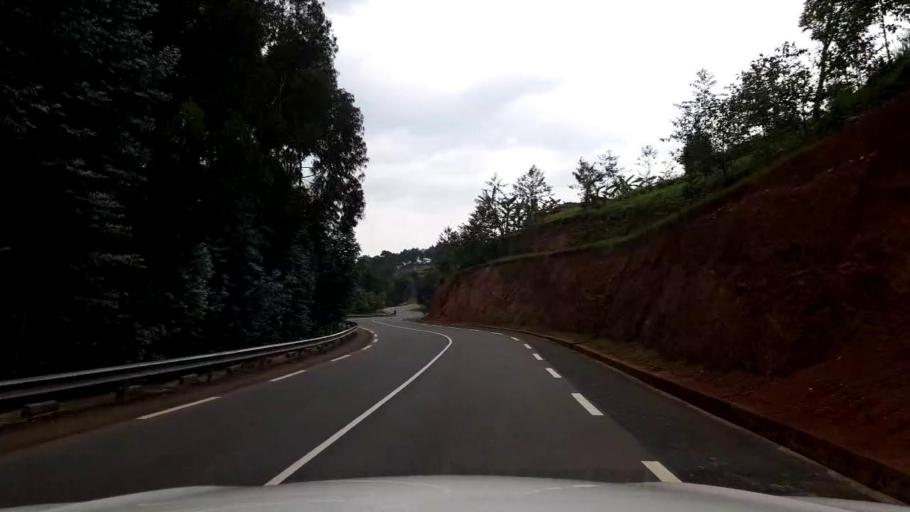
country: RW
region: Western Province
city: Kibuye
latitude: -1.8871
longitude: 29.3465
